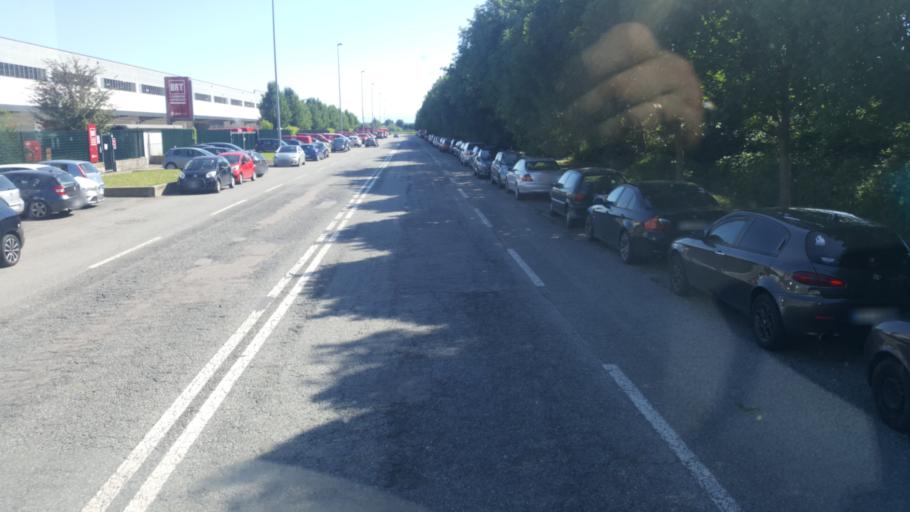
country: IT
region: Piedmont
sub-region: Provincia di Torino
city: Grugliasco
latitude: 45.0449
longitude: 7.5648
